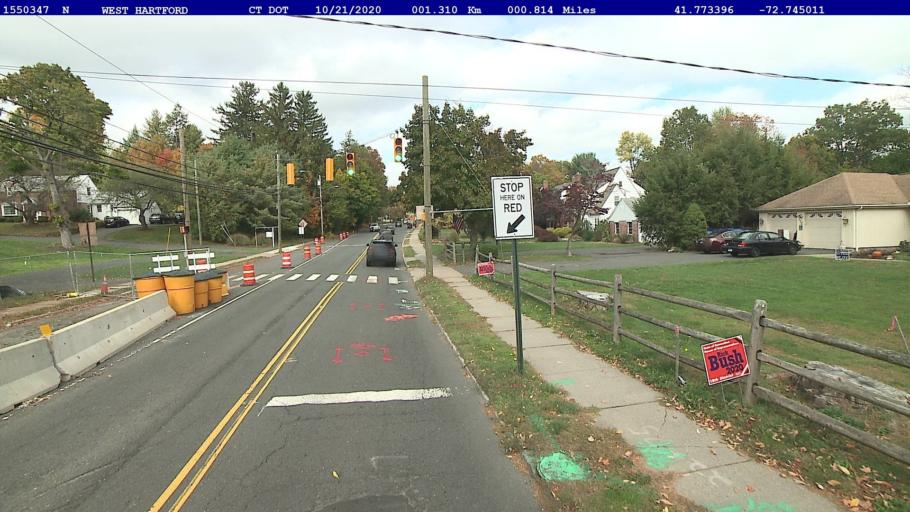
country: US
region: Connecticut
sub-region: Hartford County
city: West Hartford
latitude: 41.7734
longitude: -72.7450
